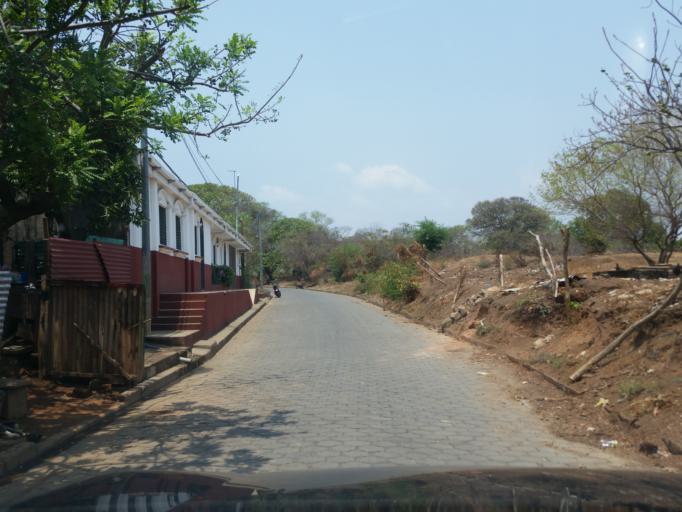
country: NI
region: Granada
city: Granada
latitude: 11.9354
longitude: -85.9729
